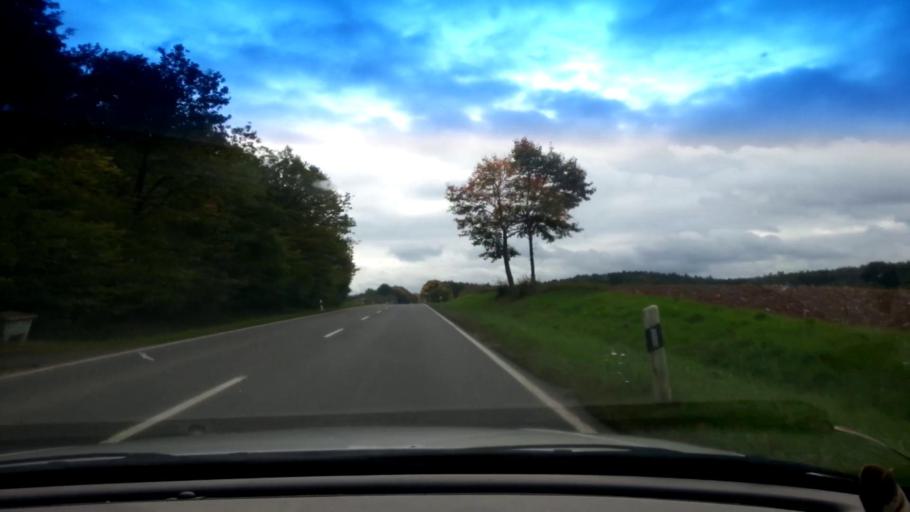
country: DE
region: Bavaria
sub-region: Upper Franconia
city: Viereth-Trunstadt
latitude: 49.9094
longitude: 10.8006
